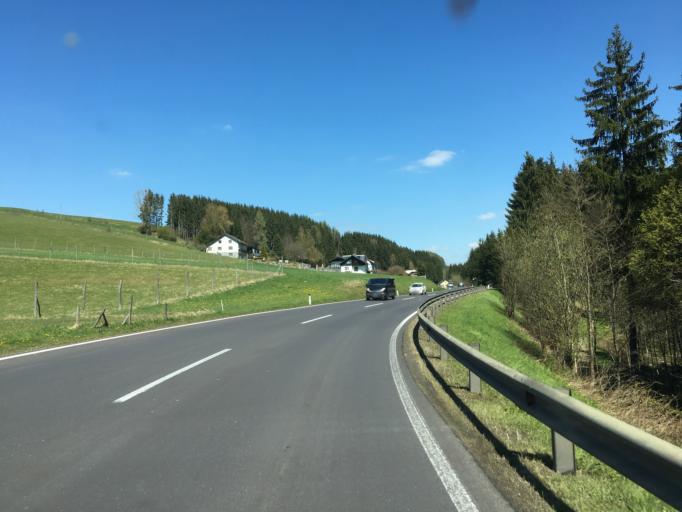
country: AT
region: Upper Austria
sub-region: Politischer Bezirk Urfahr-Umgebung
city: Zwettl an der Rodl
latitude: 48.4731
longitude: 14.2817
